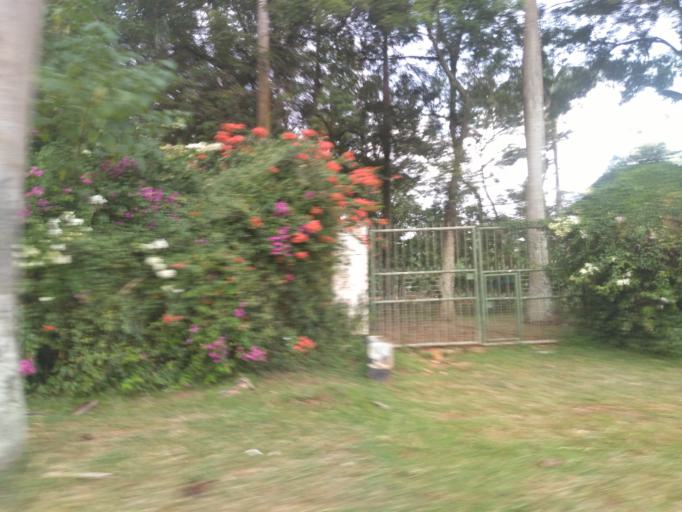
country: UG
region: Eastern Region
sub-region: Jinja District
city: Jinja
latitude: 0.4163
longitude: 33.2027
